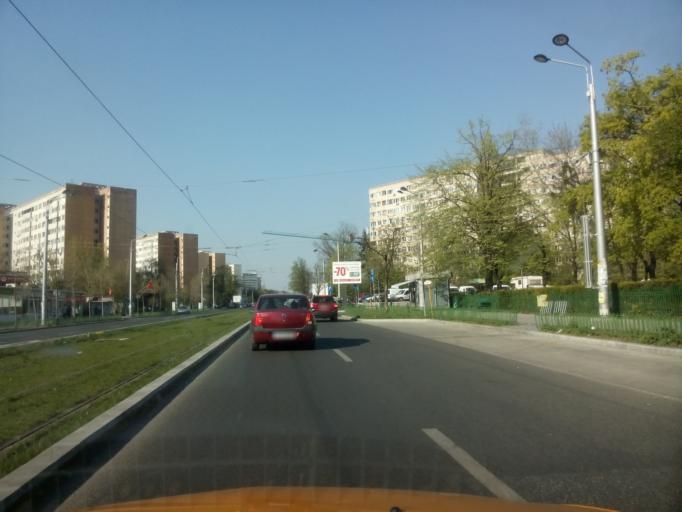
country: RO
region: Ilfov
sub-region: Comuna Popesti-Leordeni
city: Popesti-Leordeni
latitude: 44.4180
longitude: 26.1467
